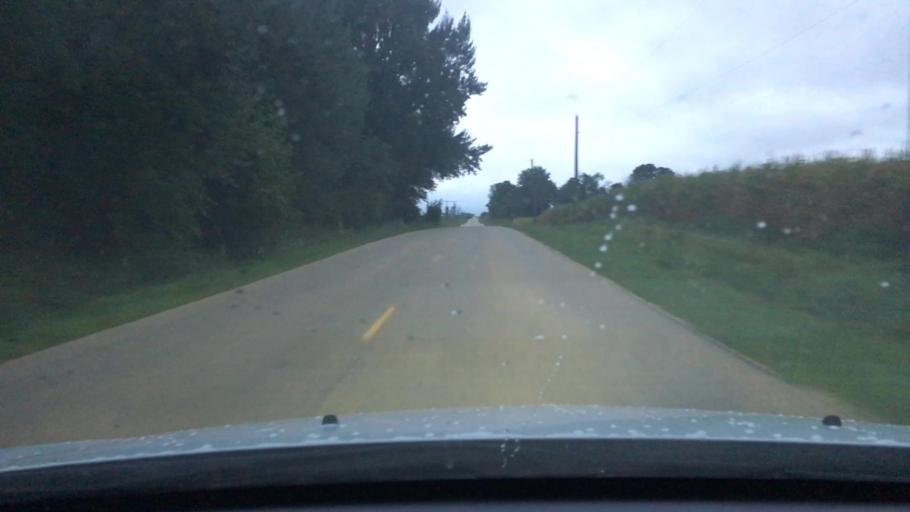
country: US
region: Illinois
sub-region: DeKalb County
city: Malta
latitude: 41.8679
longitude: -88.9615
